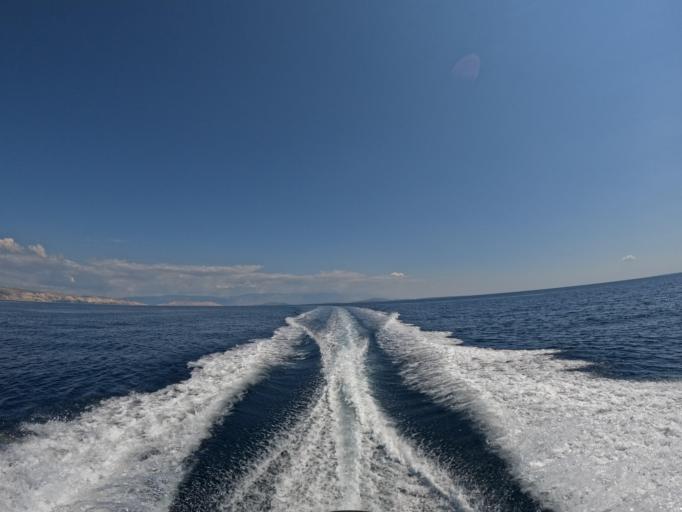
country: HR
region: Primorsko-Goranska
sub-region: Grad Krk
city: Krk
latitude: 44.9310
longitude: 14.5219
